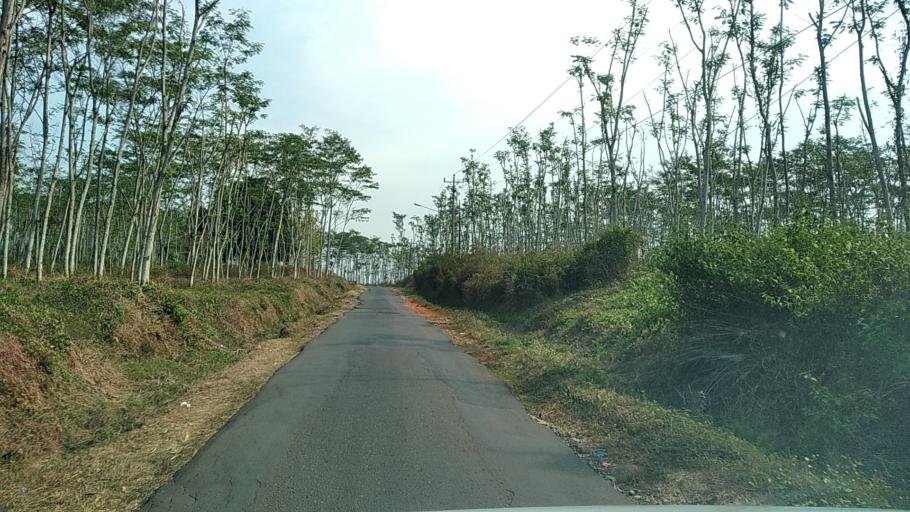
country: ID
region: Central Java
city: Semarang
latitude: -7.0328
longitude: 110.3148
